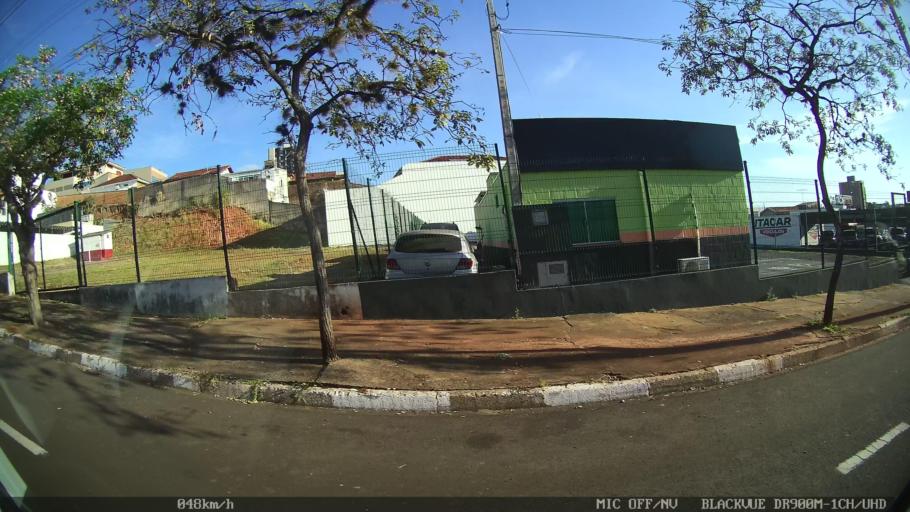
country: BR
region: Sao Paulo
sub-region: Franca
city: Franca
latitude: -20.5294
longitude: -47.4007
